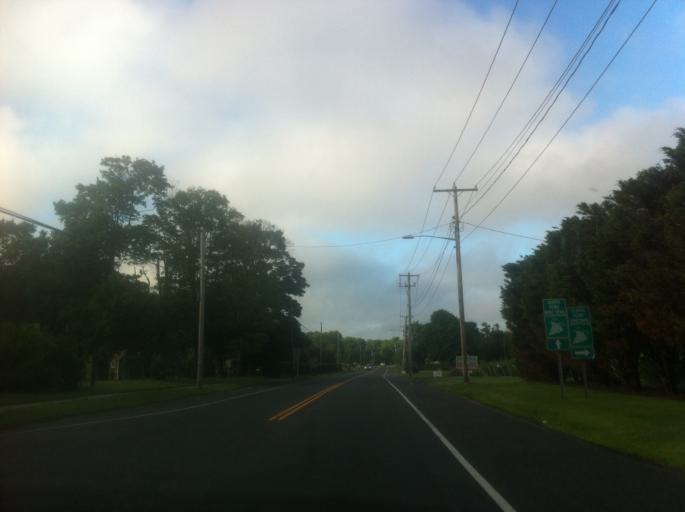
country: US
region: New York
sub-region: Suffolk County
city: Jamesport
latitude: 40.9561
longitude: -72.5738
